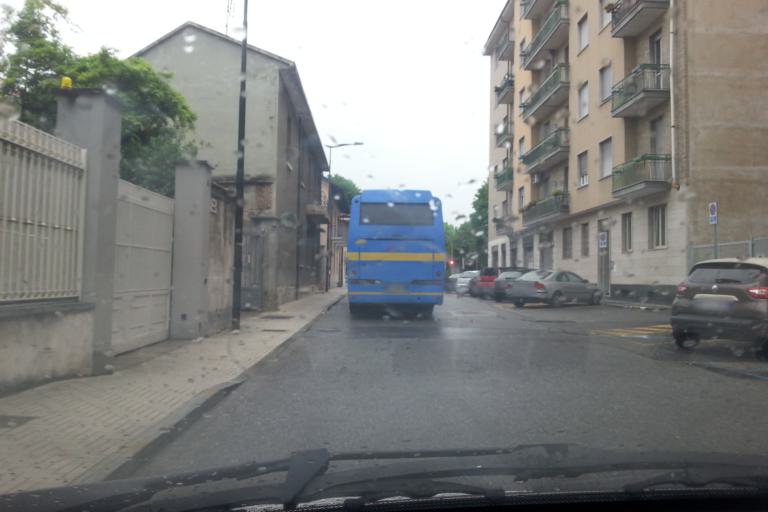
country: IT
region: Piedmont
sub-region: Provincia di Torino
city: Rivoli
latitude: 45.0697
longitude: 7.5239
